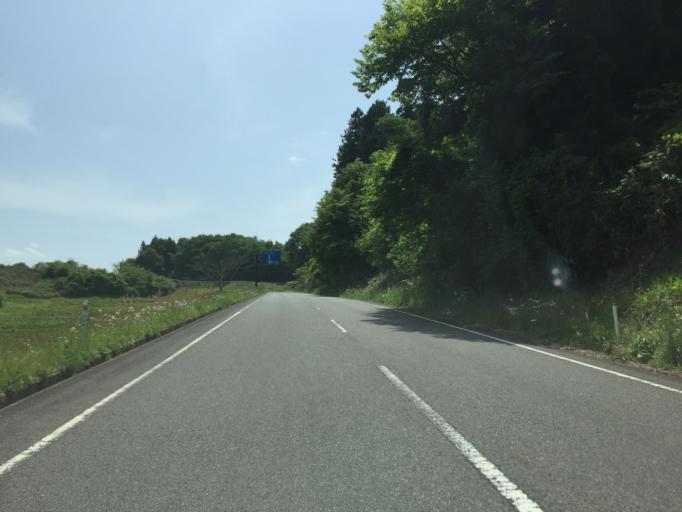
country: JP
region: Fukushima
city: Ishikawa
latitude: 37.1760
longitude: 140.5063
